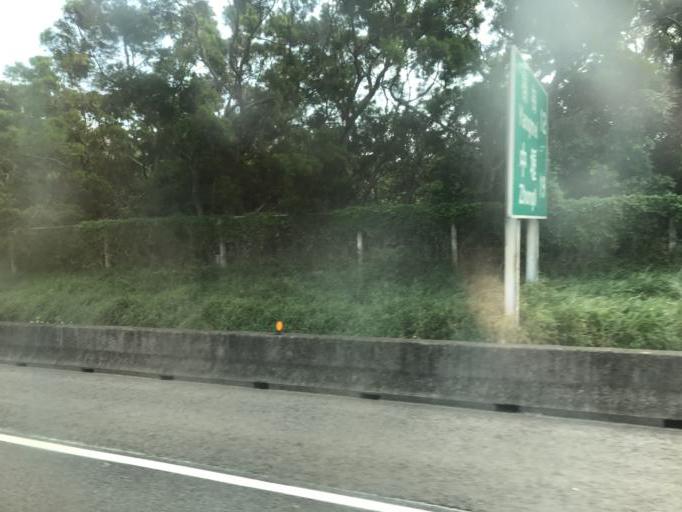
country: TW
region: Taiwan
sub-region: Hsinchu
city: Zhubei
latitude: 24.8767
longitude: 121.0462
